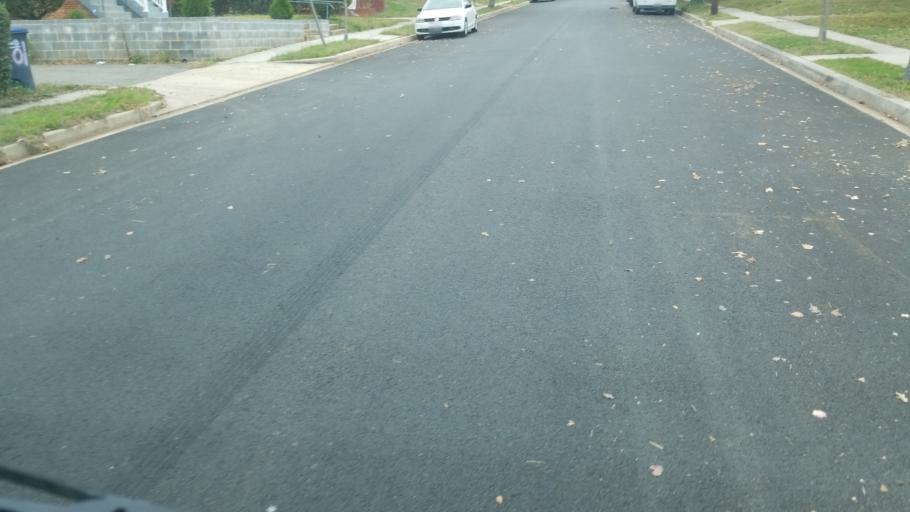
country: US
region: Maryland
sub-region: Prince George's County
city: Capitol Heights
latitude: 38.8908
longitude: -76.9297
